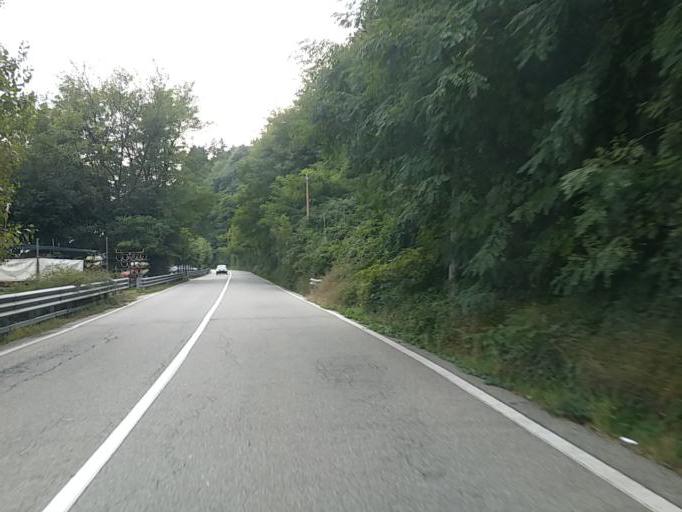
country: IT
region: Piedmont
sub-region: Provincia Verbano-Cusio-Ossola
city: Ghiffa
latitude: 45.9673
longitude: 8.6249
